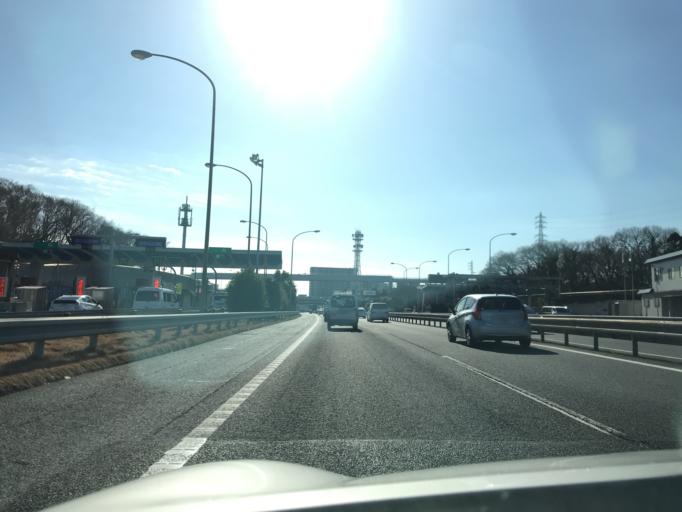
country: JP
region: Chiba
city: Chiba
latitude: 35.6440
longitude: 140.1118
